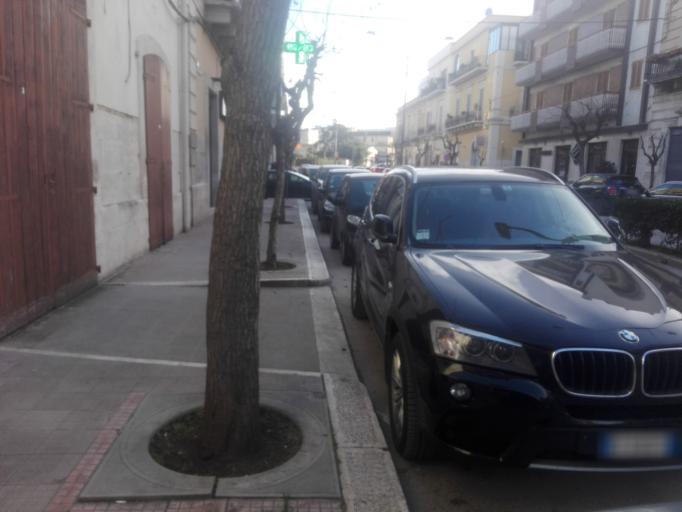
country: IT
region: Apulia
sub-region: Provincia di Bari
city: Corato
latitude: 41.1528
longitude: 16.4167
